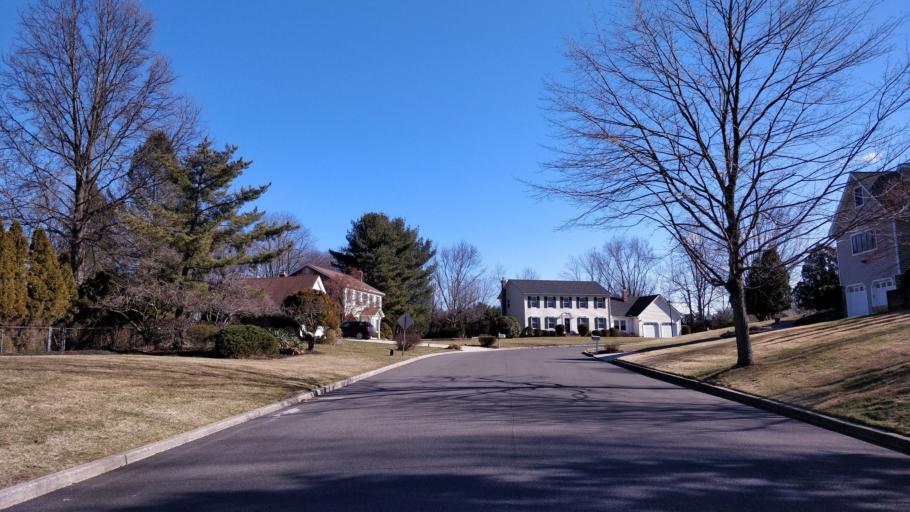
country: US
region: New York
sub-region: Suffolk County
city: Setauket-East Setauket
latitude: 40.9297
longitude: -73.1067
